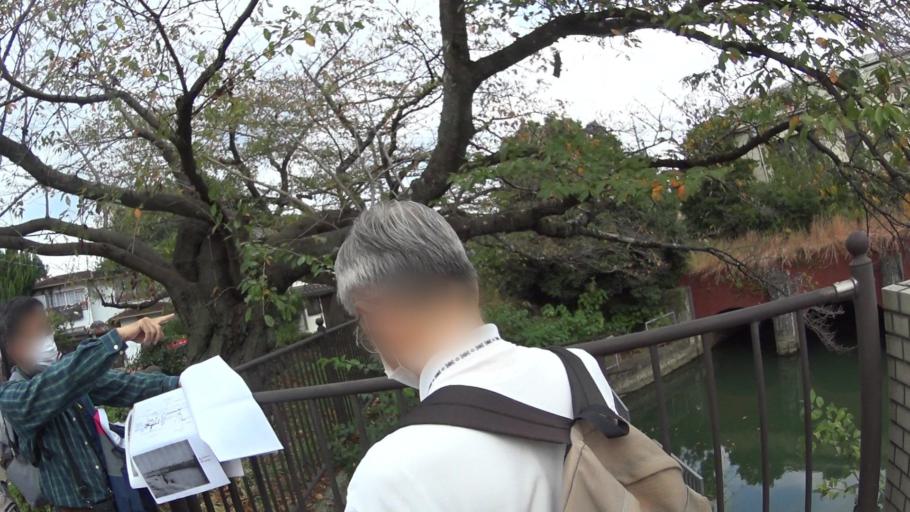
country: JP
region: Osaka
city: Kishiwada
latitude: 34.5132
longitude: 135.3458
